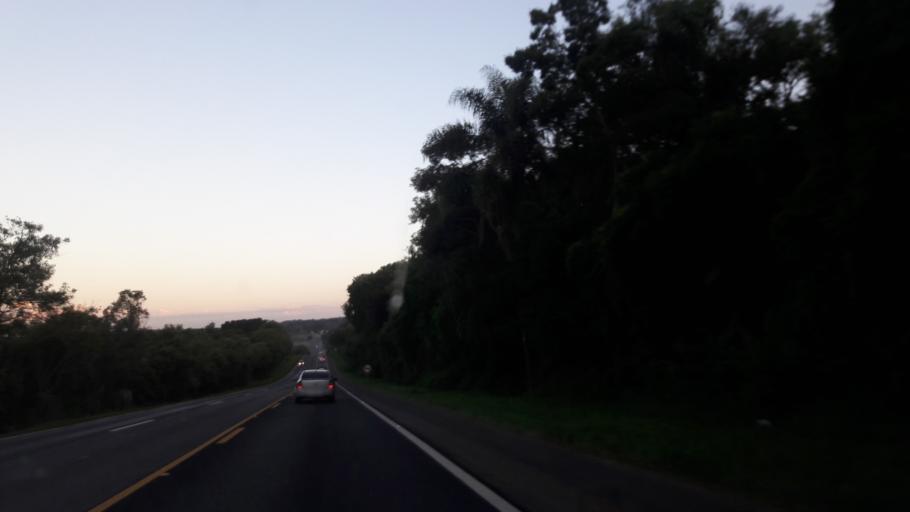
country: BR
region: Parana
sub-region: Palmeira
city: Palmeira
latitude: -25.4645
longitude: -50.2480
